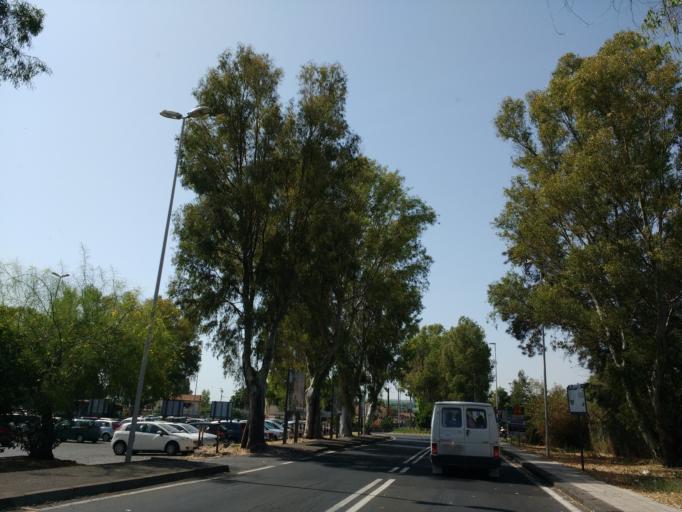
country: IT
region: Sicily
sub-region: Catania
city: Catania
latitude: 37.4746
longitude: 15.0661
